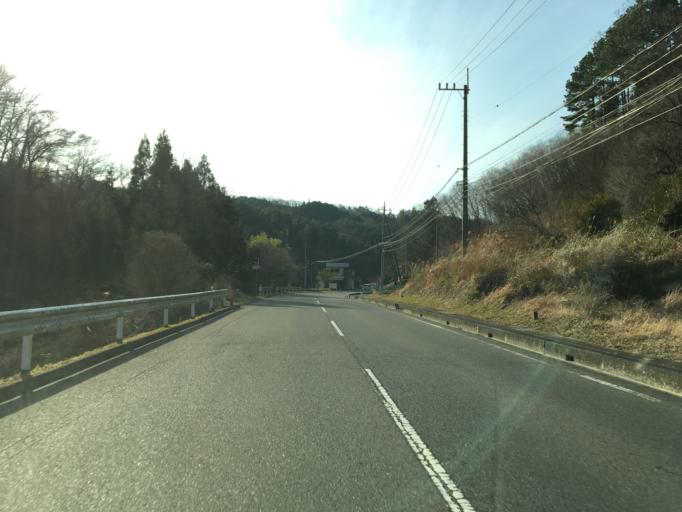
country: JP
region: Ibaraki
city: Daigo
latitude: 36.7513
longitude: 140.4444
